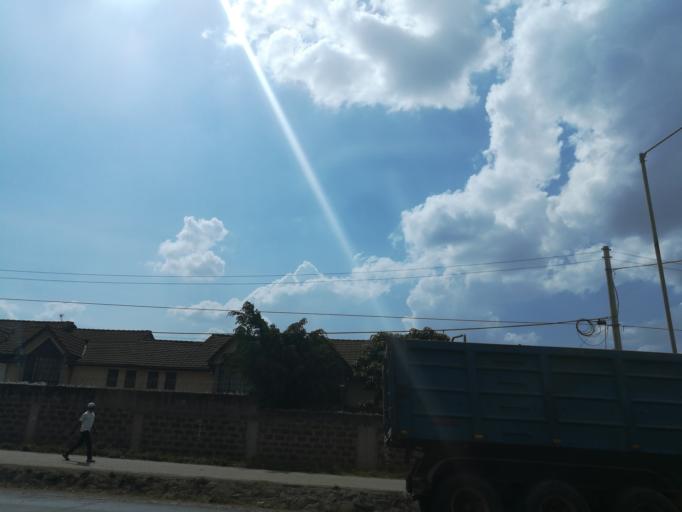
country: KE
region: Nairobi Area
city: Pumwani
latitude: -1.3195
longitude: 36.8523
